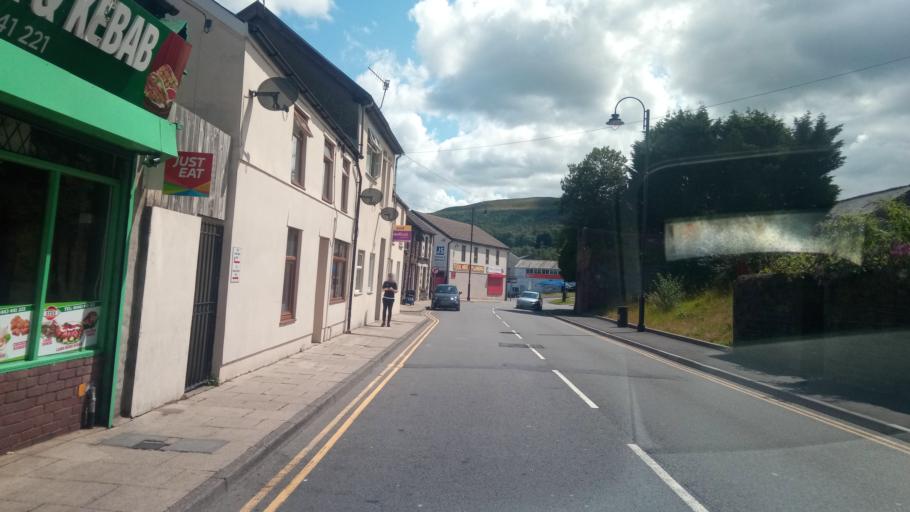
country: GB
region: Wales
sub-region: Rhondda Cynon Taf
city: Tonypandy
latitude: 51.6195
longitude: -3.4509
